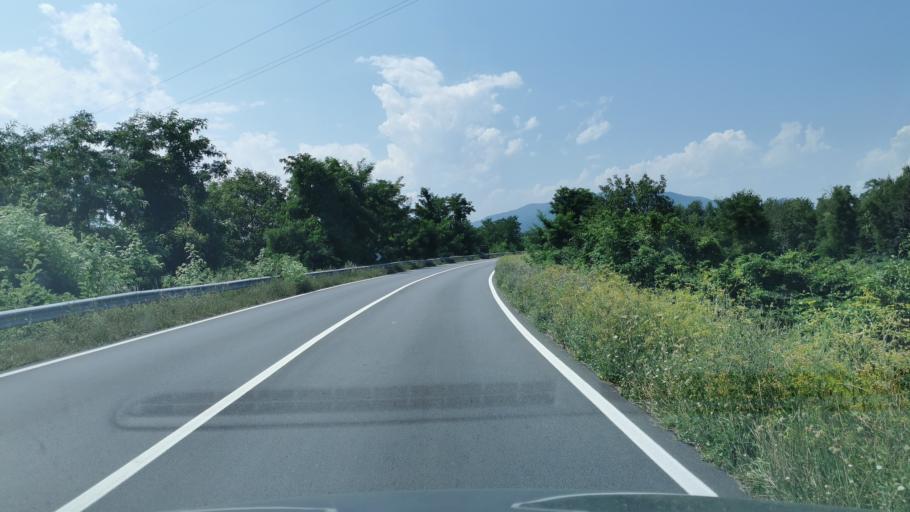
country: IT
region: Piedmont
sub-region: Provincia di Cuneo
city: Borgo San Dalmazzo
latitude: 44.3310
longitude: 7.5125
